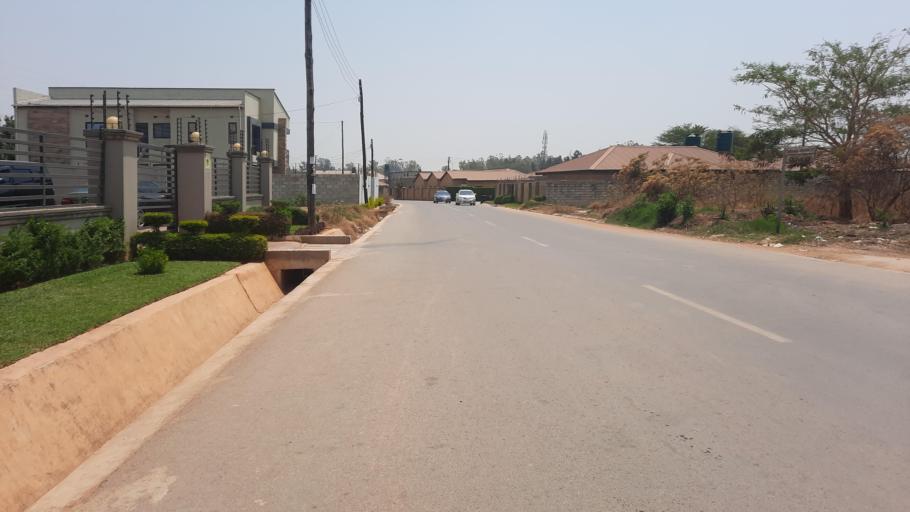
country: ZM
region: Lusaka
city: Lusaka
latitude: -15.3929
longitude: 28.3850
